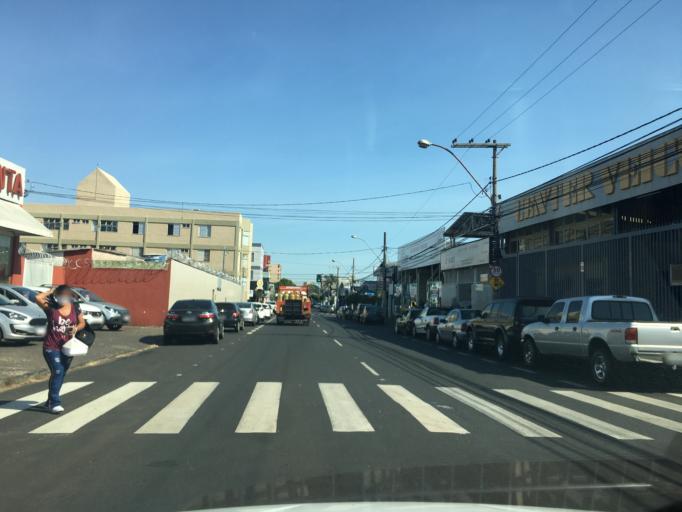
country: BR
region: Minas Gerais
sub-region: Uberlandia
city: Uberlandia
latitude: -18.8965
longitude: -48.2634
